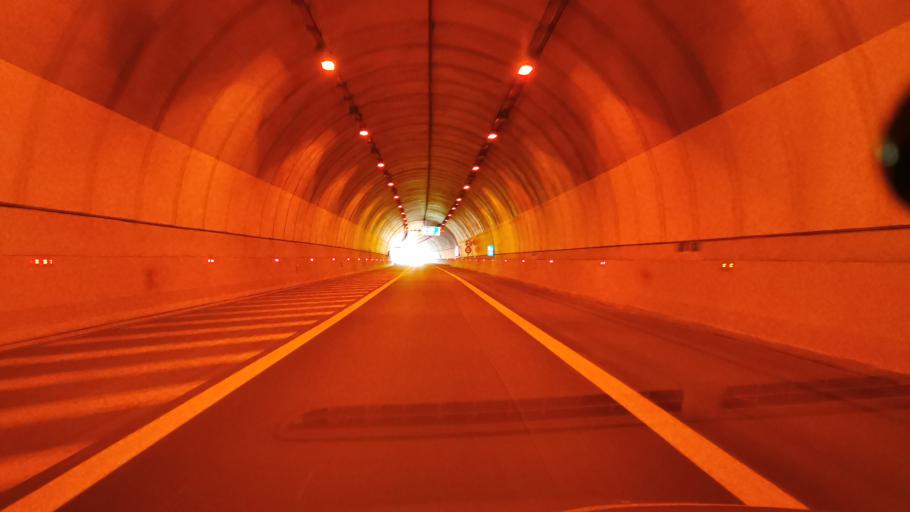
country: IT
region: Piedmont
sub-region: Provincia di Cuneo
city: Cuneo
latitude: 44.4275
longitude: 7.5670
